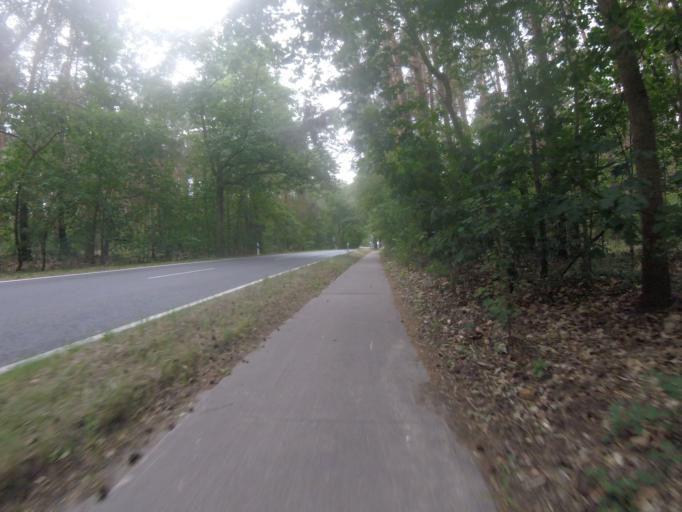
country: DE
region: Brandenburg
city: Bestensee
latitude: 52.2519
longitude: 13.6314
